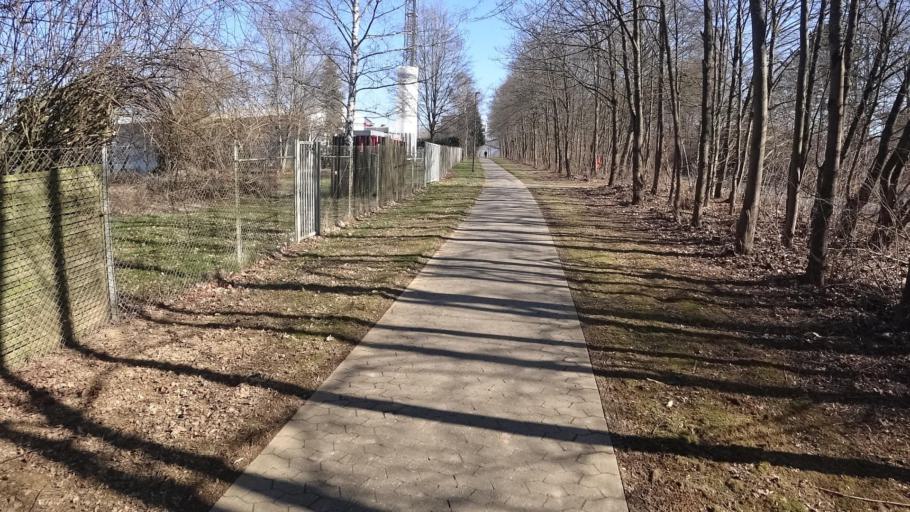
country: DE
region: Rheinland-Pfalz
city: Riesweiler
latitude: 49.9833
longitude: 7.5429
